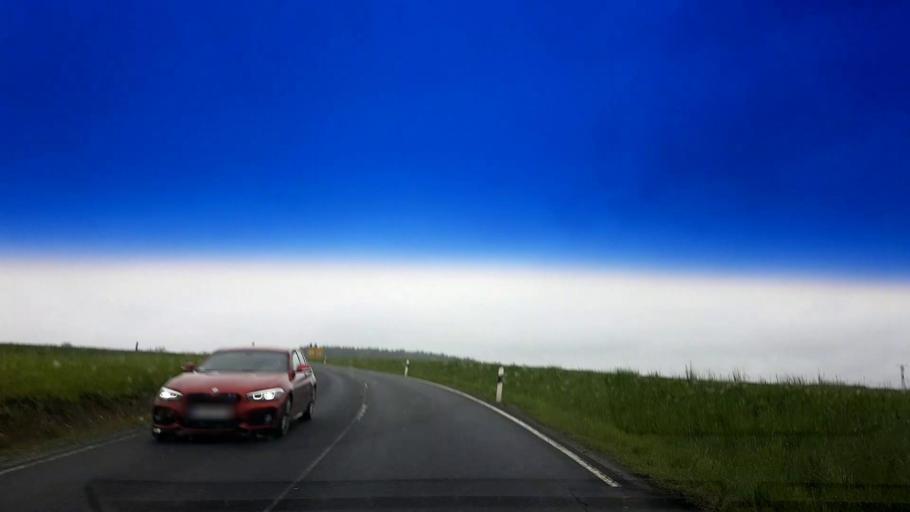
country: DE
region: Bavaria
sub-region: Upper Franconia
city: Bindlach
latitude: 50.0044
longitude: 11.6283
